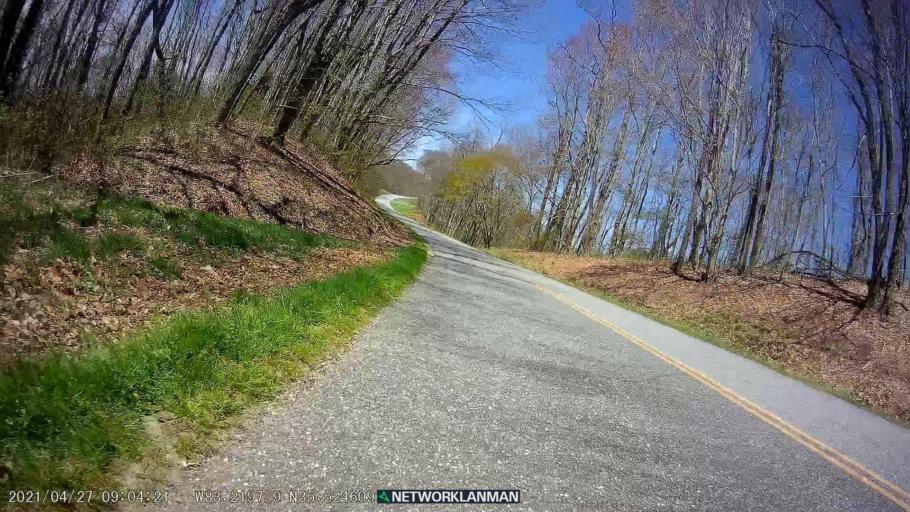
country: US
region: North Carolina
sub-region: Swain County
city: Cherokee
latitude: 35.5246
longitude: -83.2193
